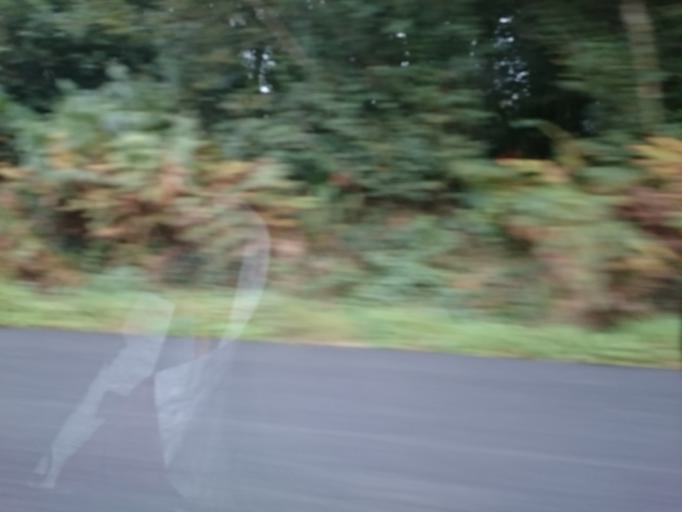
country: FR
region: Brittany
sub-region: Departement des Cotes-d'Armor
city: Belle-Isle-en-Terre
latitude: 48.5486
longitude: -3.4147
